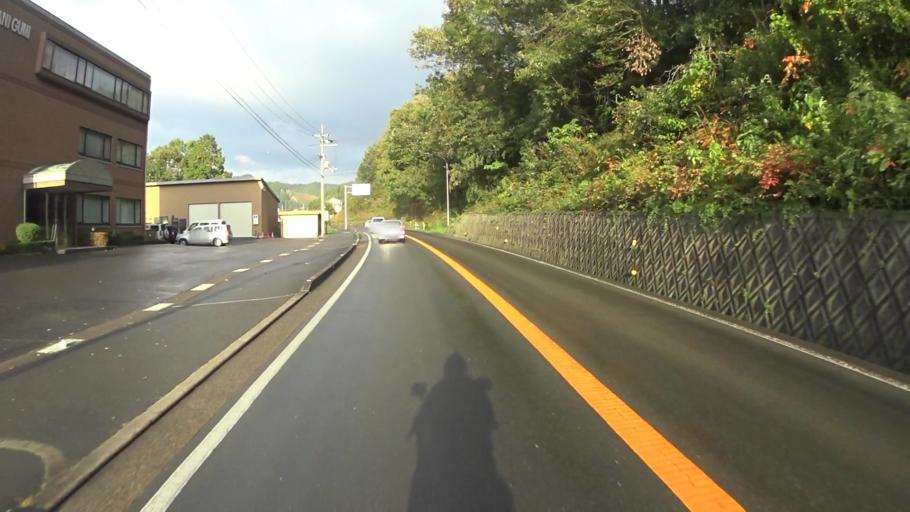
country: JP
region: Kyoto
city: Ayabe
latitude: 35.1822
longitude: 135.3756
